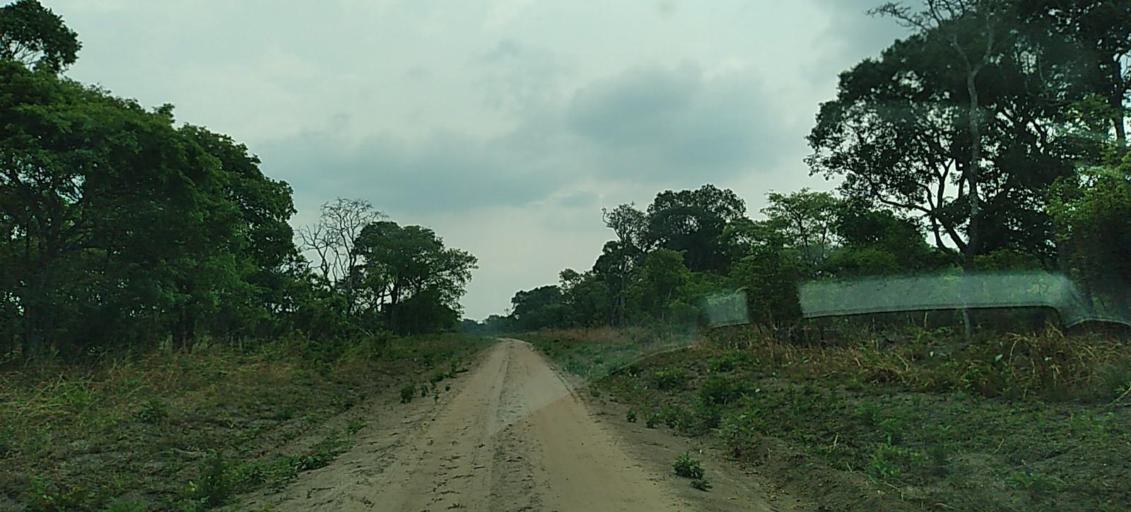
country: ZM
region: North-Western
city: Mwinilunga
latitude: -11.4067
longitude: 24.6271
